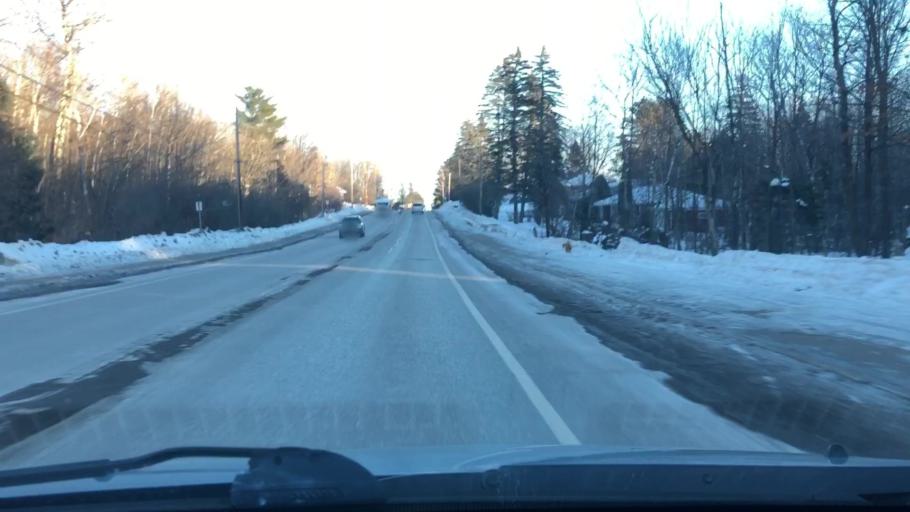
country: US
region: Minnesota
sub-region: Saint Louis County
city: Duluth
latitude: 46.8258
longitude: -92.0846
